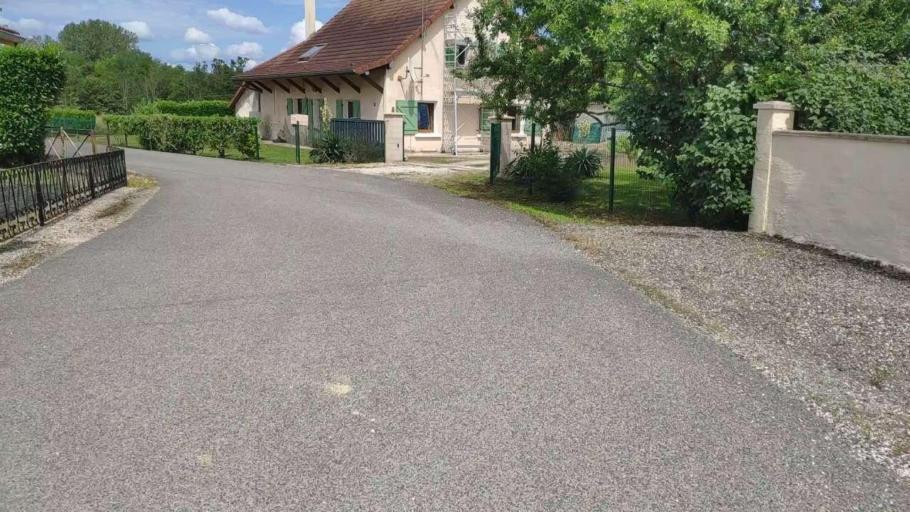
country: FR
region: Franche-Comte
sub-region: Departement du Jura
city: Chaussin
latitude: 46.8708
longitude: 5.4236
